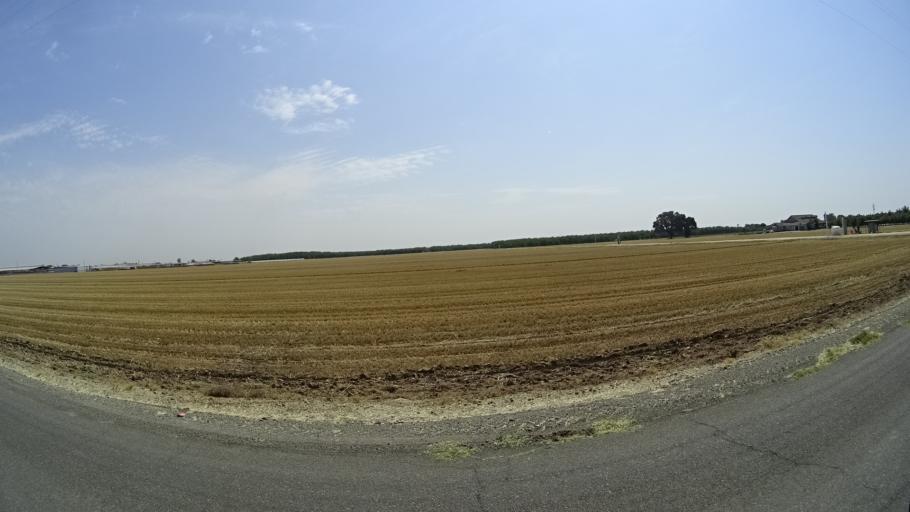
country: US
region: California
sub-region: Kings County
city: Armona
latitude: 36.3352
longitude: -119.7449
